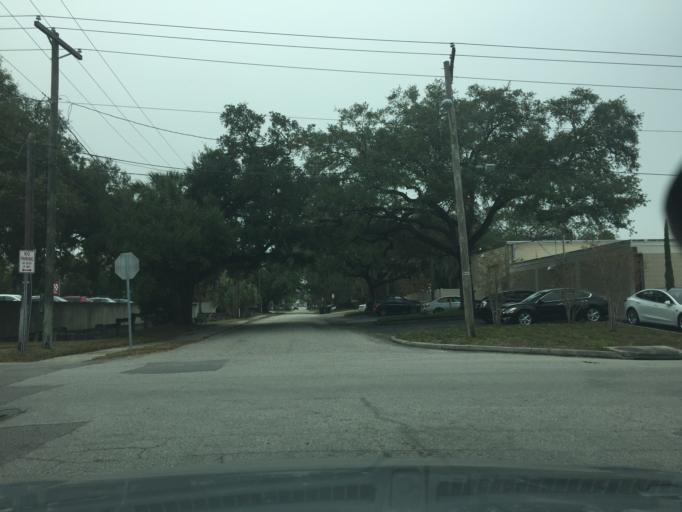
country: US
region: Florida
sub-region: Hillsborough County
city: Tampa
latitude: 27.9385
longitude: -82.4871
